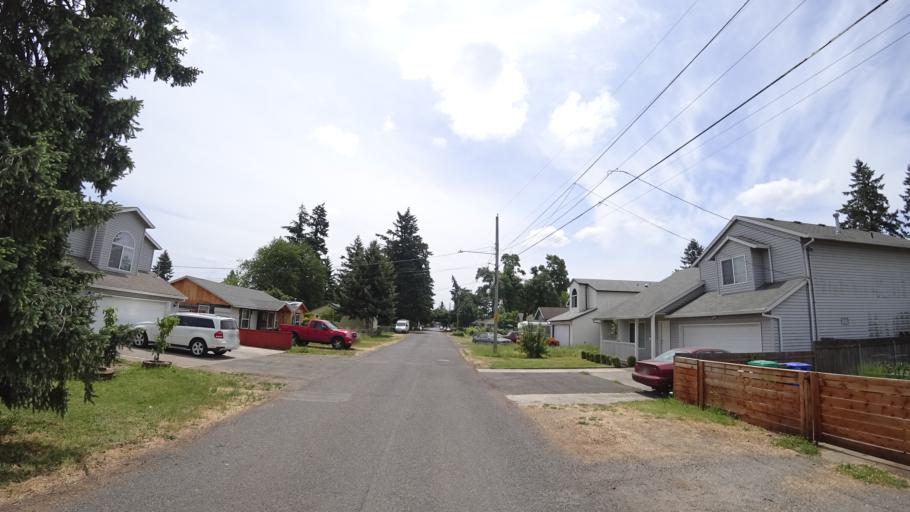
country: US
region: Oregon
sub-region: Multnomah County
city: Lents
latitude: 45.4708
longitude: -122.5923
